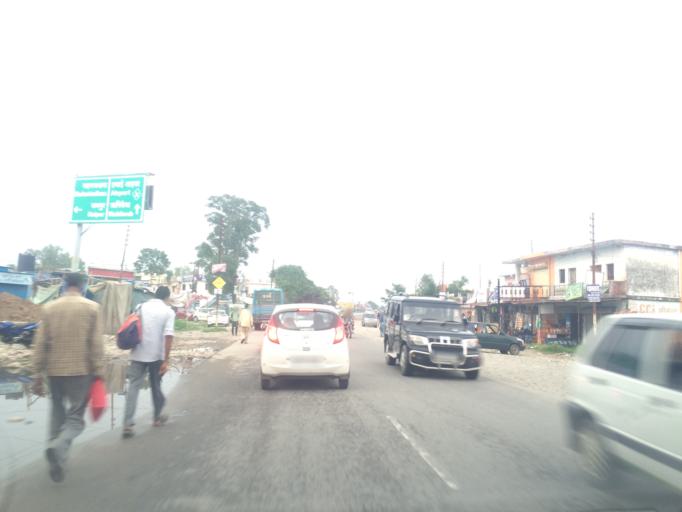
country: IN
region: Uttarakhand
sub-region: Dehradun
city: Doiwala
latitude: 30.1862
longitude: 78.1480
